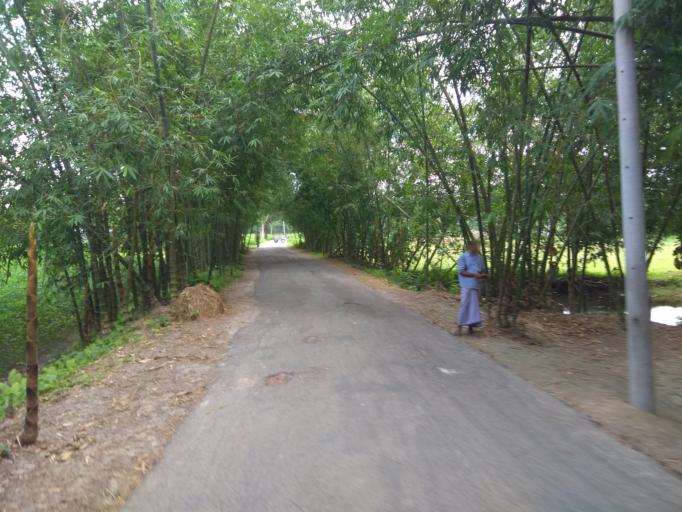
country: IN
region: West Bengal
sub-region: Koch Bihar
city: Haldibari
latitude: 26.2031
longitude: 88.9200
